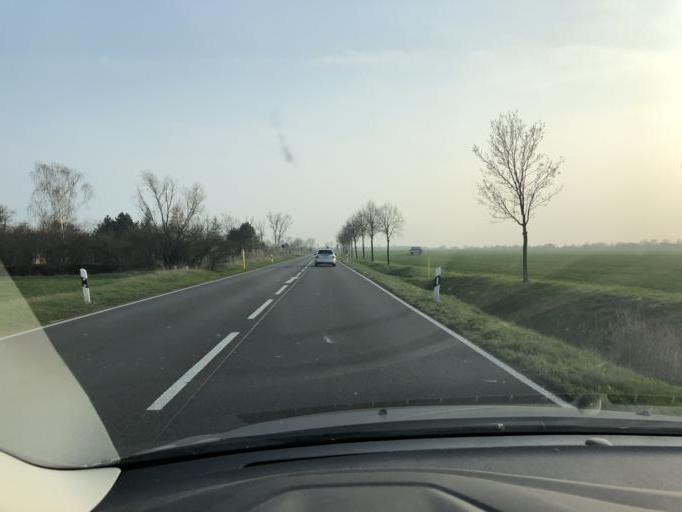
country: DE
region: Saxony
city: Dobernitz
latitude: 51.4963
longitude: 12.3354
